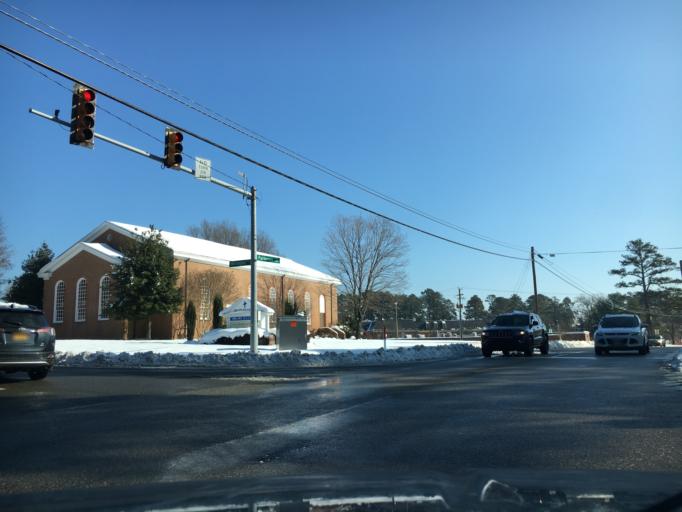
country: US
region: Virginia
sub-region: Henrico County
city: Tuckahoe
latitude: 37.5928
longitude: -77.5347
